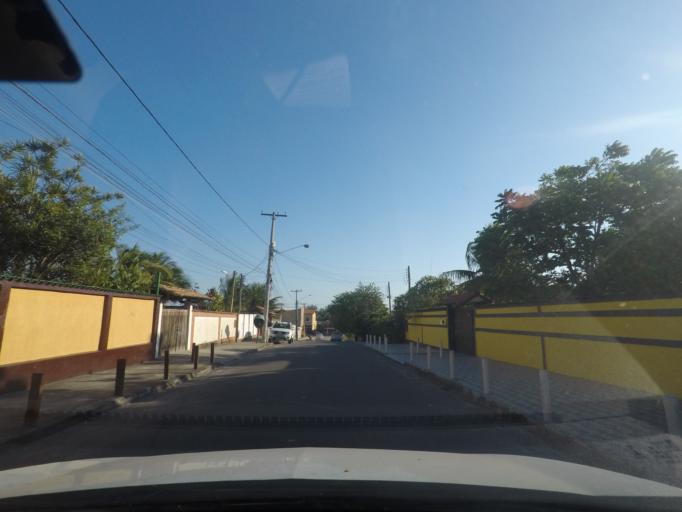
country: BR
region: Rio de Janeiro
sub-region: Marica
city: Marica
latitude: -22.9690
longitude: -42.9377
